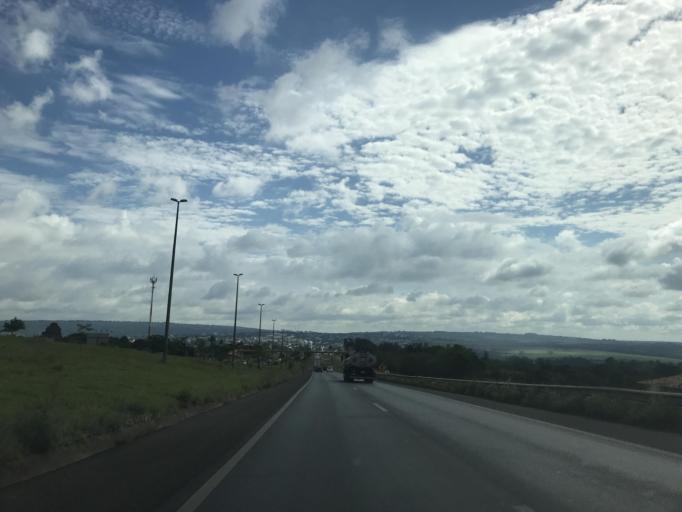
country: BR
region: Federal District
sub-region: Brasilia
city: Brasilia
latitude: -15.6789
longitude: -47.8272
